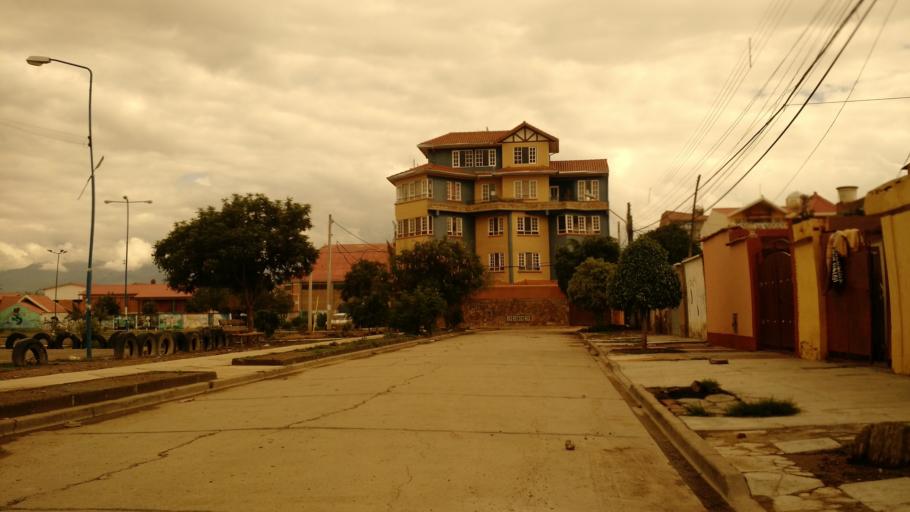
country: BO
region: Cochabamba
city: Cochabamba
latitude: -17.4340
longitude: -66.1559
